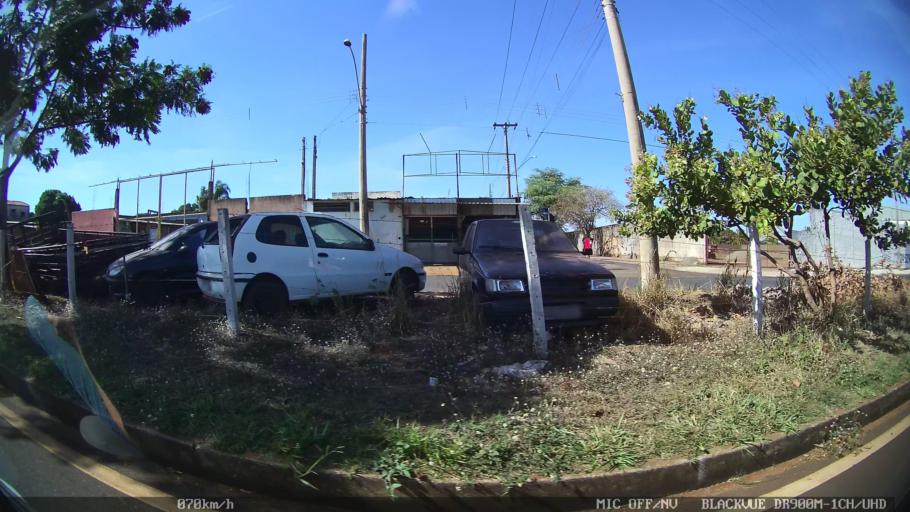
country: BR
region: Sao Paulo
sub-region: Barretos
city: Barretos
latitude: -20.5516
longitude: -48.5913
